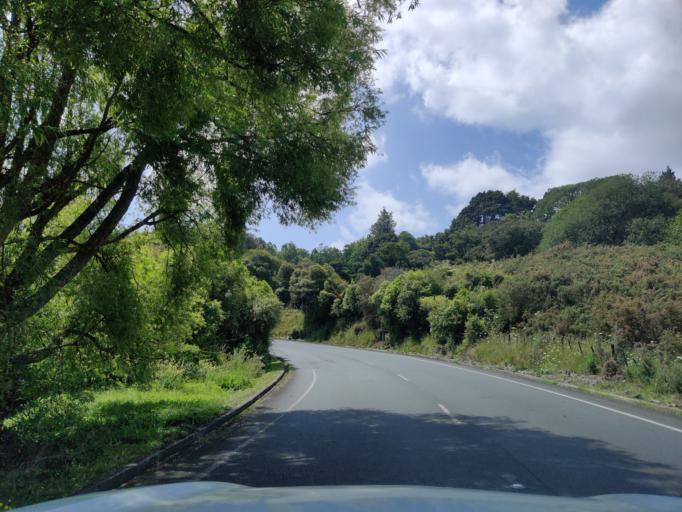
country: NZ
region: Auckland
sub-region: Auckland
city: Pukekohe East
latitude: -37.2148
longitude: 174.9505
